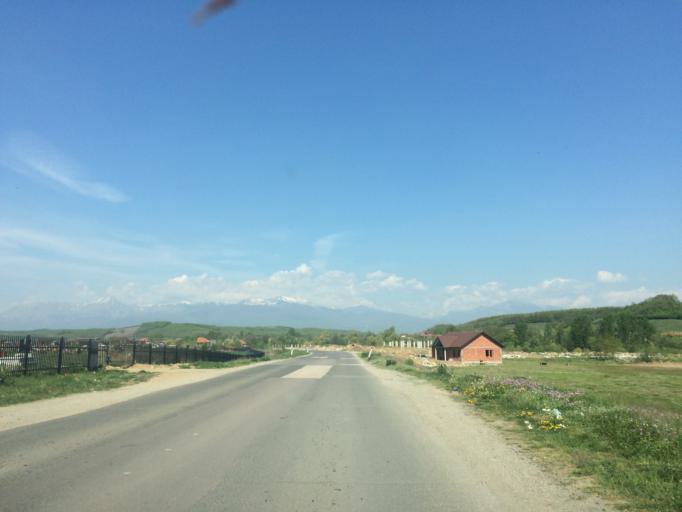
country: XK
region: Gjakova
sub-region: Komuna e Gjakoves
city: Gjakove
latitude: 42.3724
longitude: 20.4102
